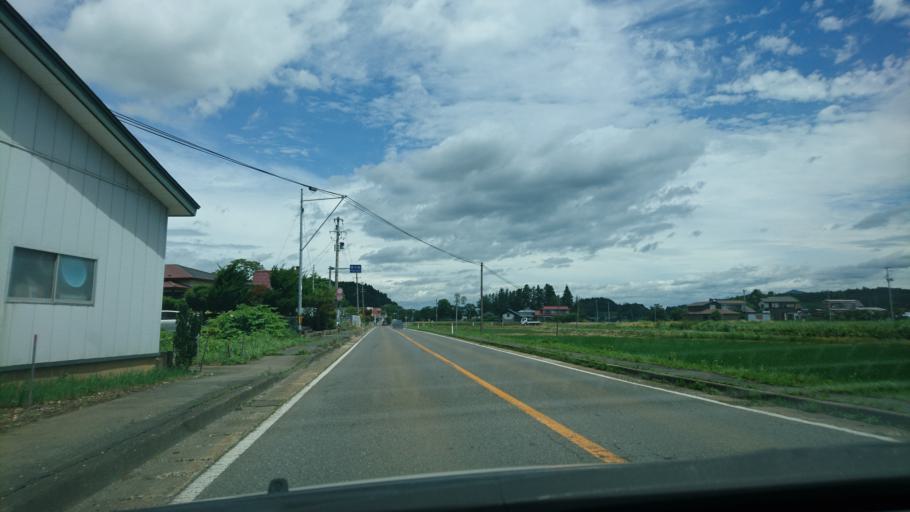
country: JP
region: Iwate
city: Morioka-shi
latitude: 39.5540
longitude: 141.1782
